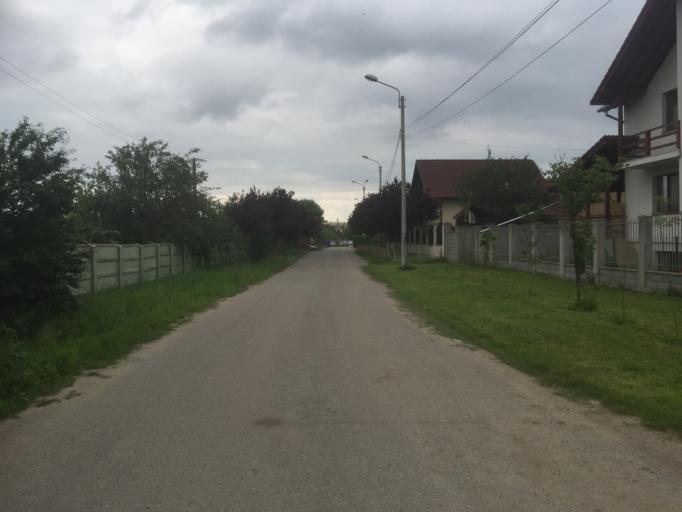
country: RO
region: Timis
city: Timisoara
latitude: 45.7541
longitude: 21.1945
